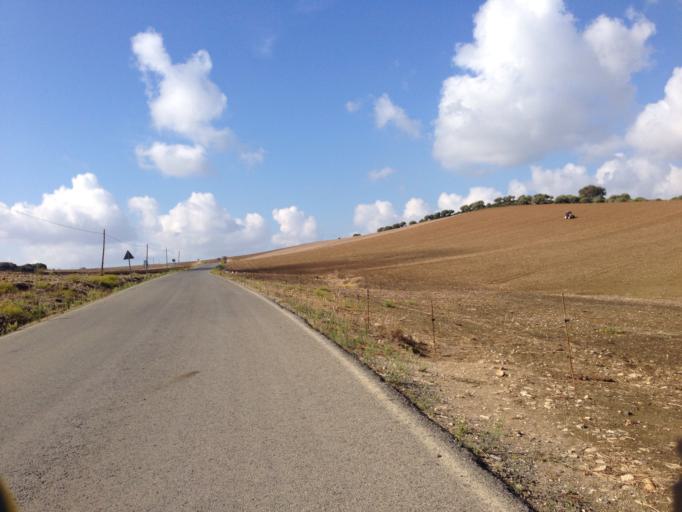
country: ES
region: Andalusia
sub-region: Provincia de Cadiz
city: Vejer de la Frontera
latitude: 36.3569
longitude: -5.9810
